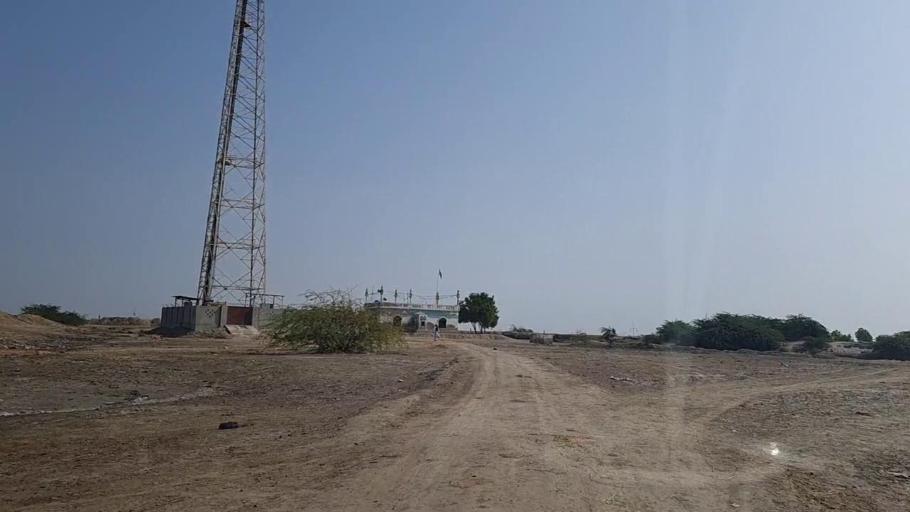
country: PK
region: Sindh
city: Chuhar Jamali
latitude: 24.1645
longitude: 67.9008
